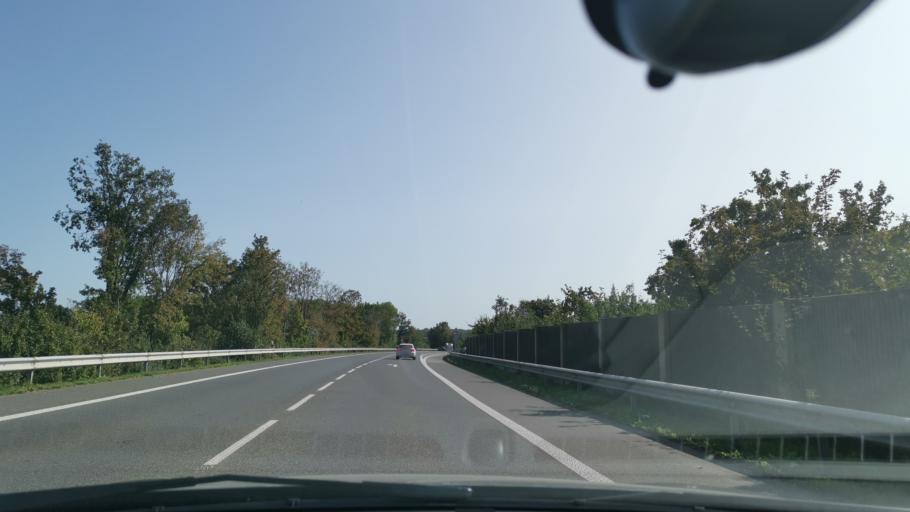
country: DE
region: North Rhine-Westphalia
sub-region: Regierungsbezirk Dusseldorf
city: Neubrueck
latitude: 51.1347
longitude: 6.6294
